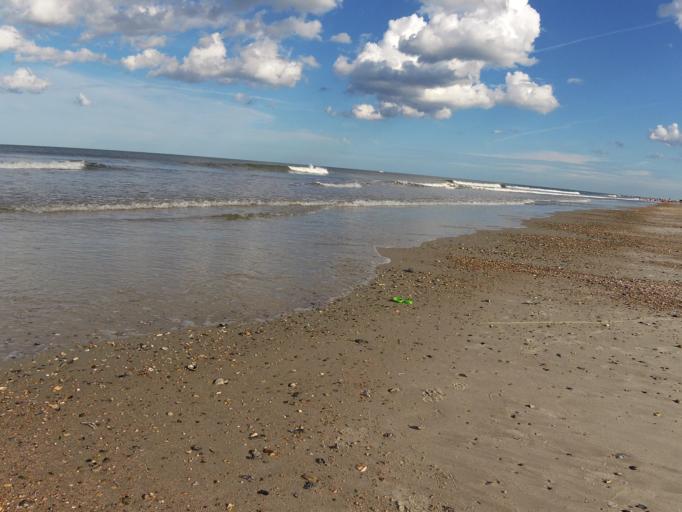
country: US
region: Florida
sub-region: Nassau County
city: Fernandina Beach
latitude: 30.6736
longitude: -81.4292
